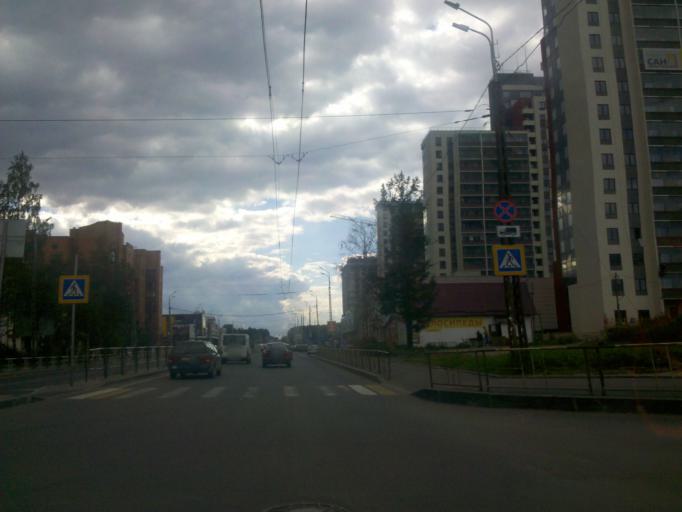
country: RU
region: Republic of Karelia
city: Petrozavodsk
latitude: 61.7845
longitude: 34.3272
